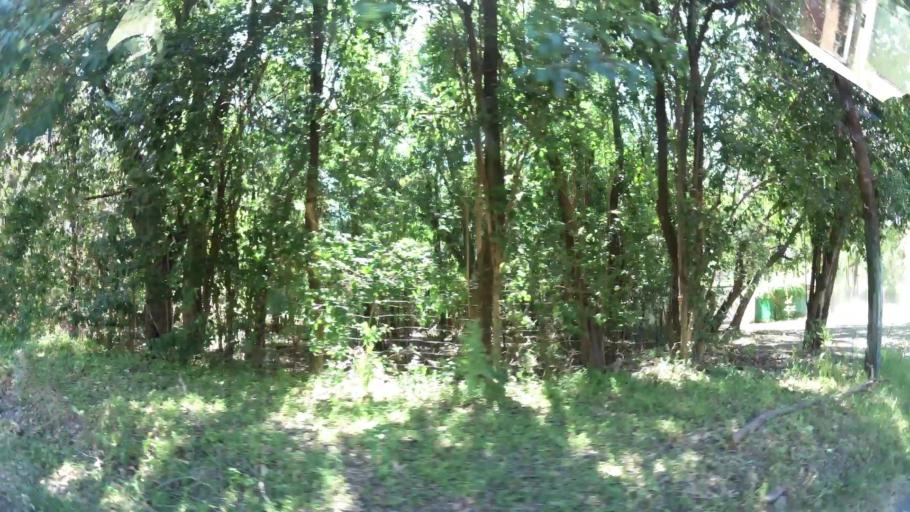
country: AR
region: Cordoba
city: Villa Allende
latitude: -31.2816
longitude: -64.2939
